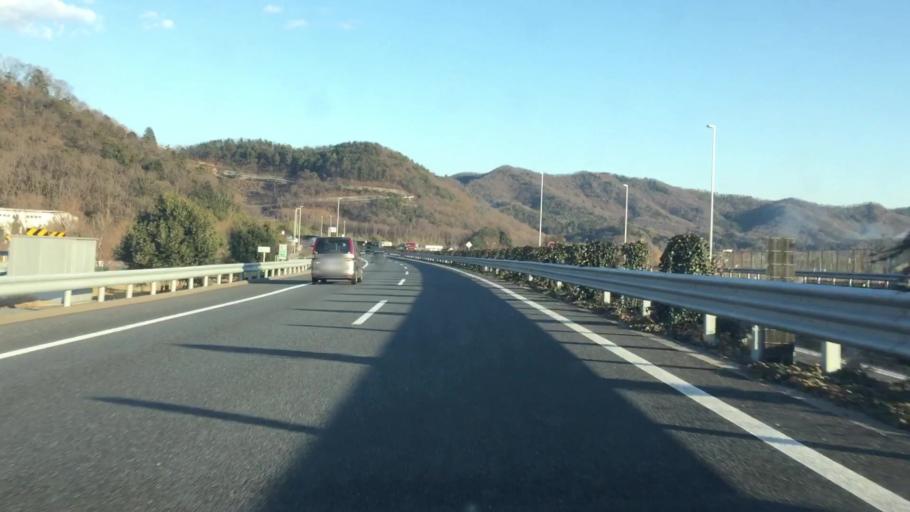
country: JP
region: Tochigi
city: Ashikaga
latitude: 36.3626
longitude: 139.4817
